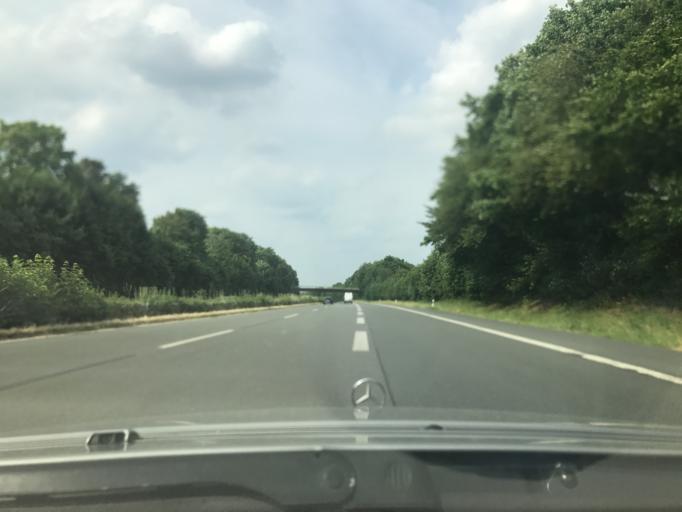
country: DE
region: North Rhine-Westphalia
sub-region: Regierungsbezirk Arnsberg
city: Unna
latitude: 51.5090
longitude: 7.7032
